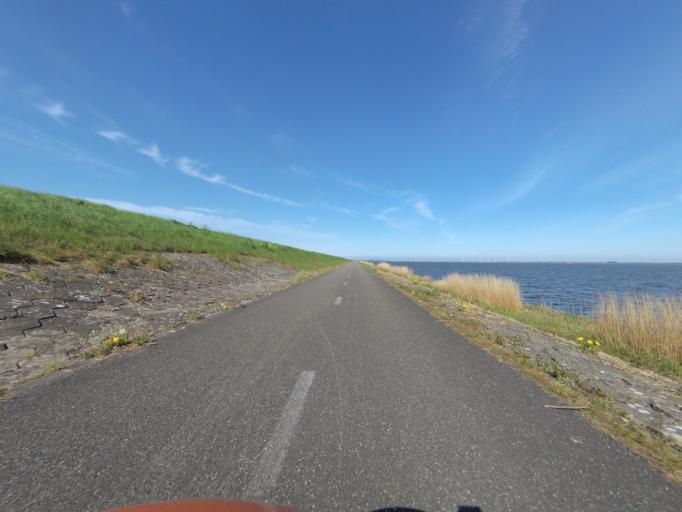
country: NL
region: Flevoland
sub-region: Gemeente Dronten
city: Dronten
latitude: 52.5851
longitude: 5.7341
